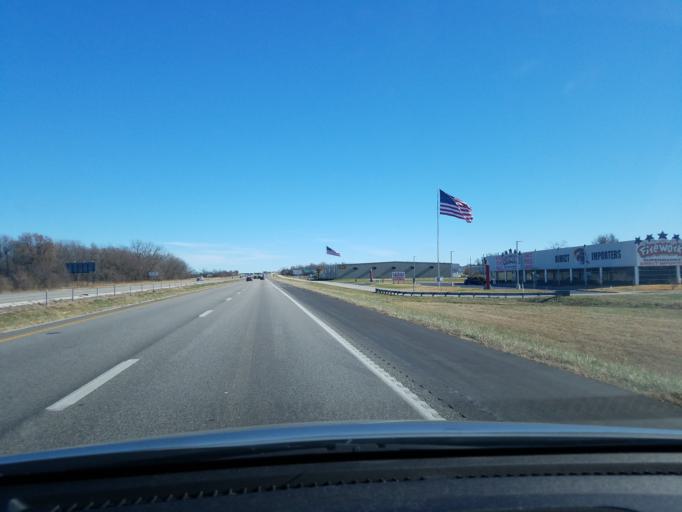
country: US
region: Missouri
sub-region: Greene County
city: Strafford
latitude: 37.2501
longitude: -93.2008
